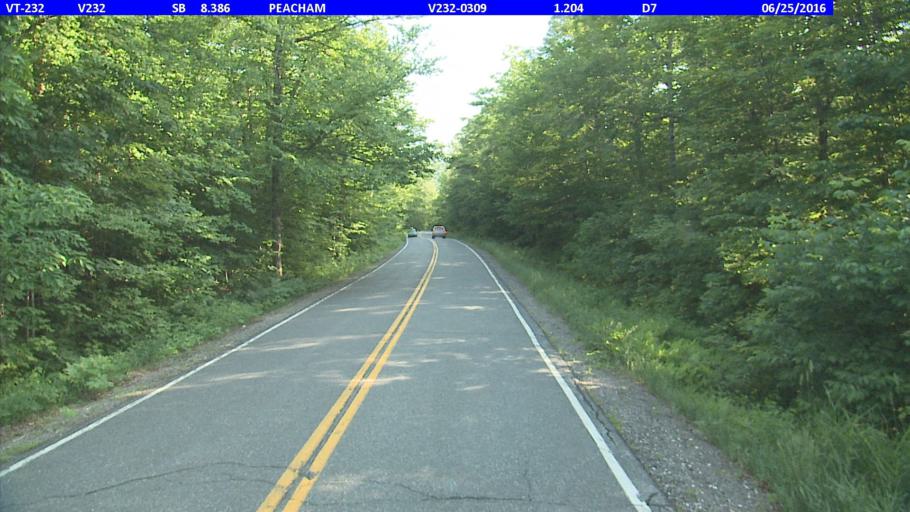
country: US
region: Vermont
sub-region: Caledonia County
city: Hardwick
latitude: 44.3124
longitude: -72.3007
